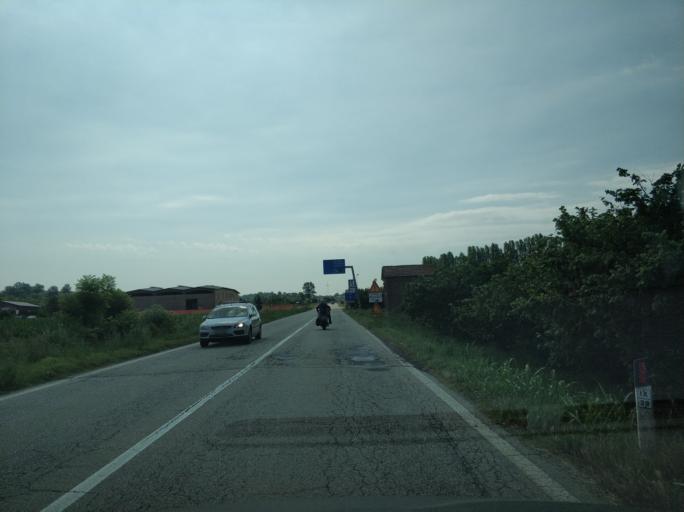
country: IT
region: Piedmont
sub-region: Provincia di Cuneo
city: Monta
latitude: 44.8257
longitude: 7.9390
